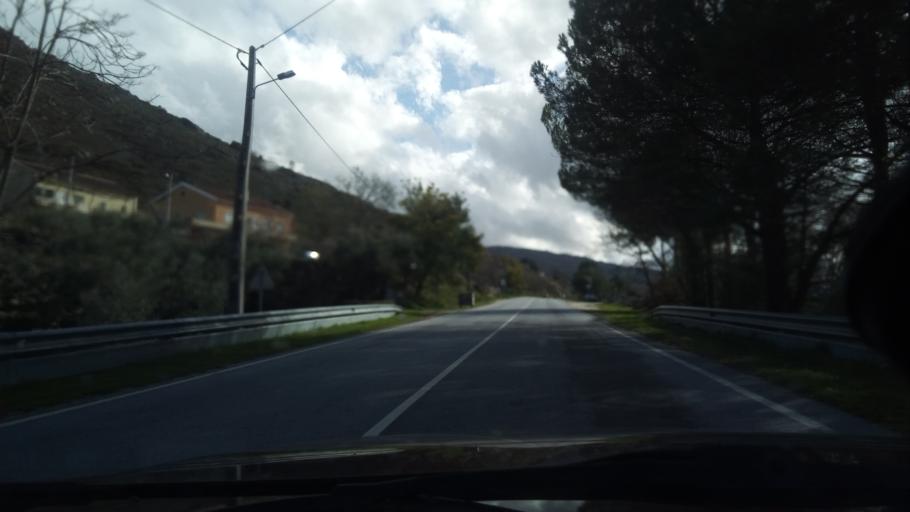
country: PT
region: Guarda
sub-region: Guarda
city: Guarda
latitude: 40.5797
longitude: -7.2948
